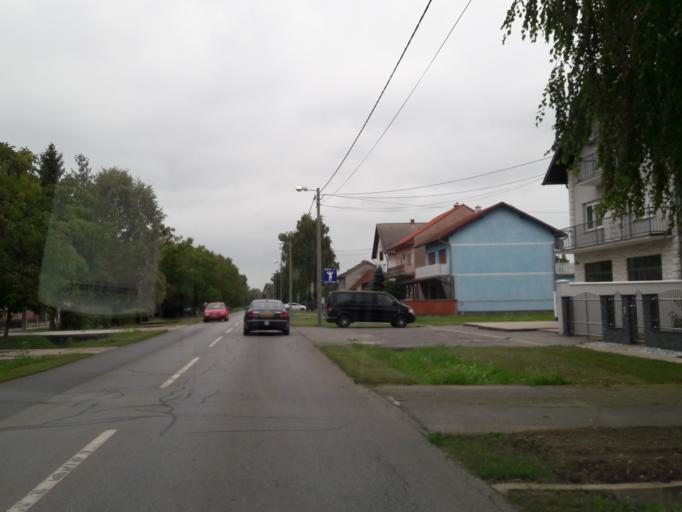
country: HR
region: Osjecko-Baranjska
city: Tenja
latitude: 45.5156
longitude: 18.7319
